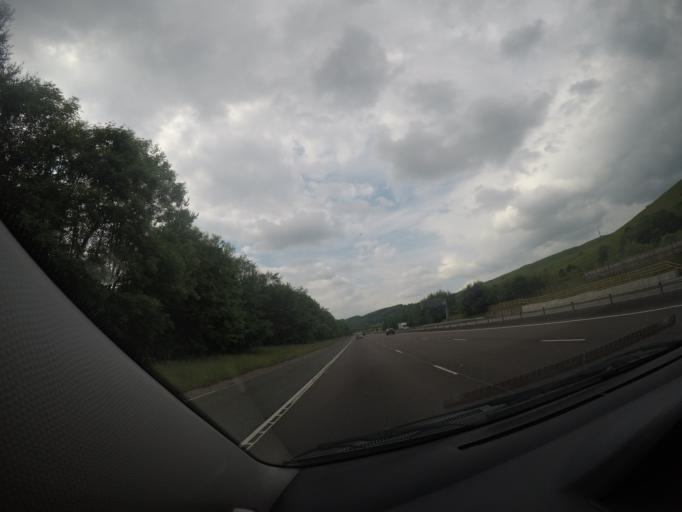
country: GB
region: Scotland
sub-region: Dumfries and Galloway
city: Moffat
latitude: 55.3336
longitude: -3.4795
